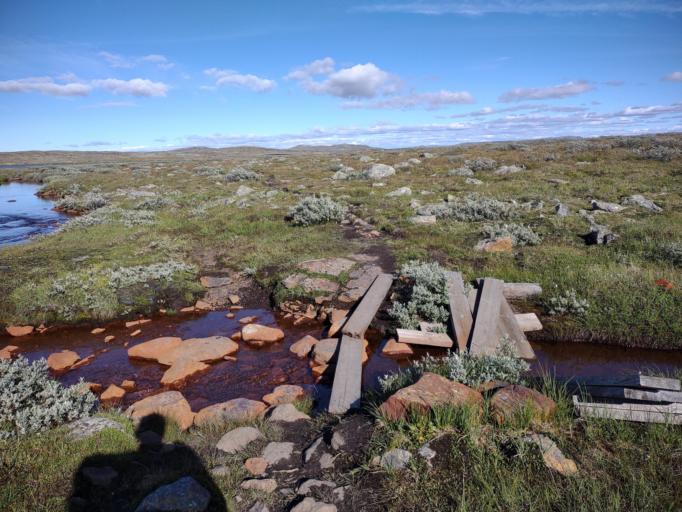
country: NO
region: Hordaland
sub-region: Eidfjord
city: Eidfjord
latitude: 60.1743
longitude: 7.4544
